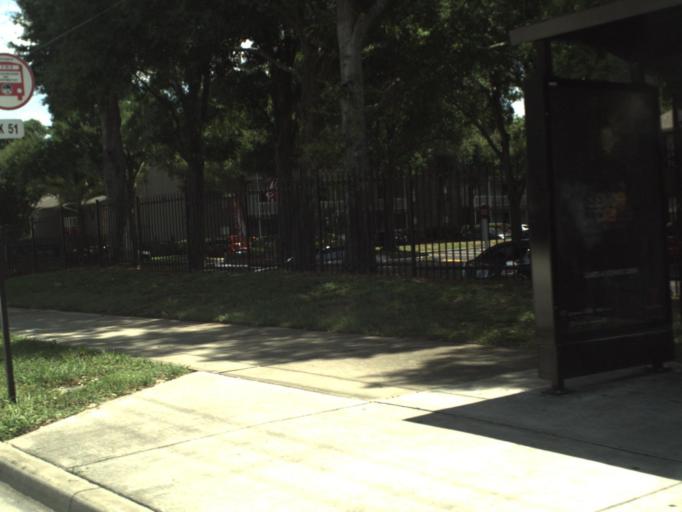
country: US
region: Florida
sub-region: Orange County
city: Conway
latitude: 28.5173
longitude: -81.3309
